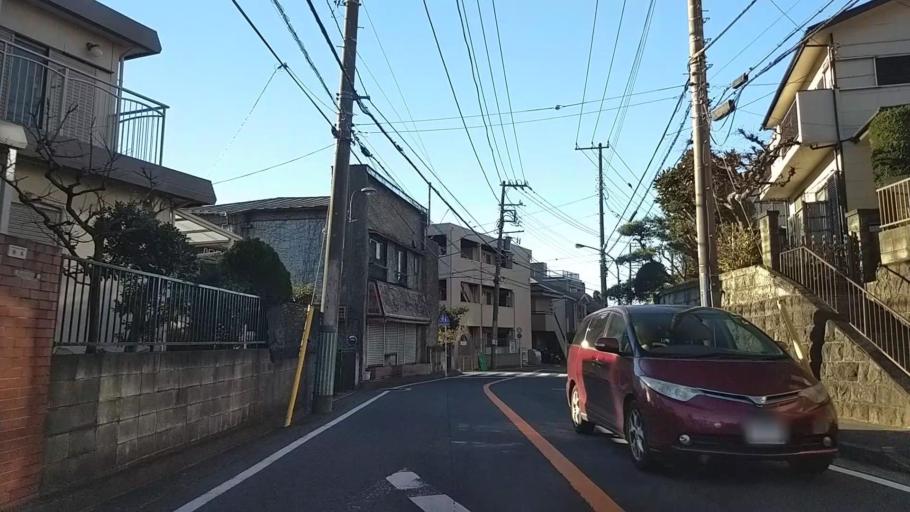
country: JP
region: Kanagawa
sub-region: Kawasaki-shi
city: Kawasaki
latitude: 35.4986
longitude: 139.6690
